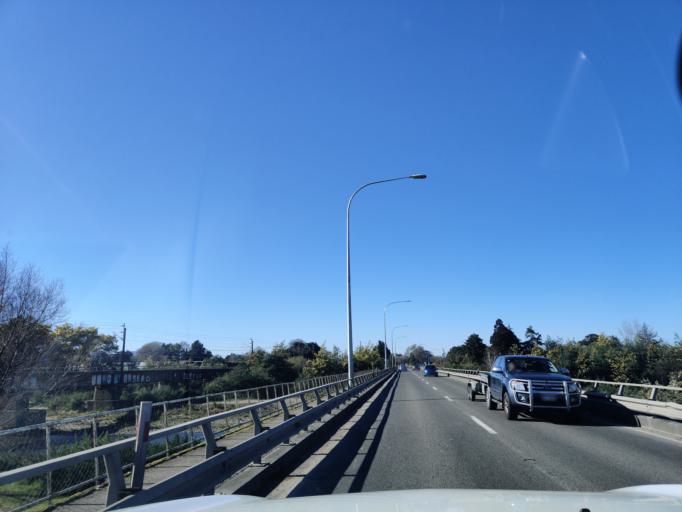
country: NZ
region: Manawatu-Wanganui
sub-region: Palmerston North City
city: Palmerston North
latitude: -40.2380
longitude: 175.5770
